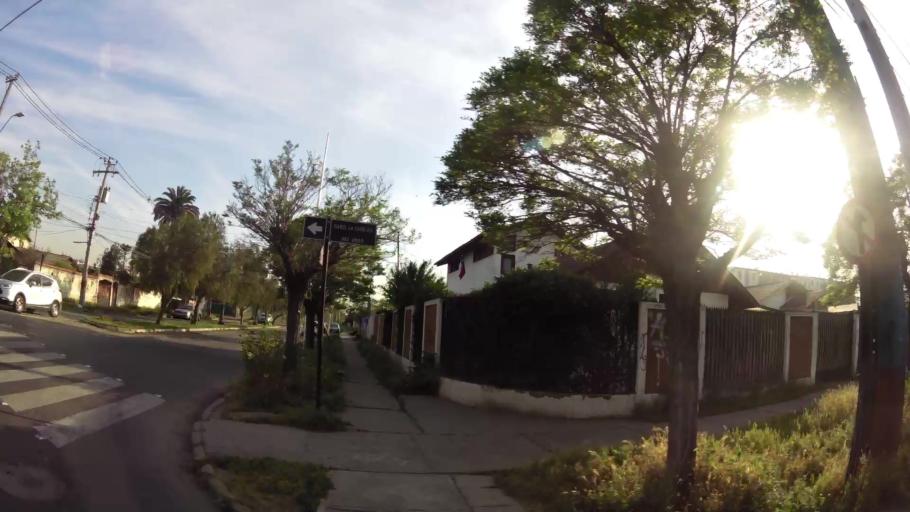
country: CL
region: Santiago Metropolitan
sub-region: Provincia de Santiago
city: La Pintana
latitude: -33.5268
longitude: -70.6728
